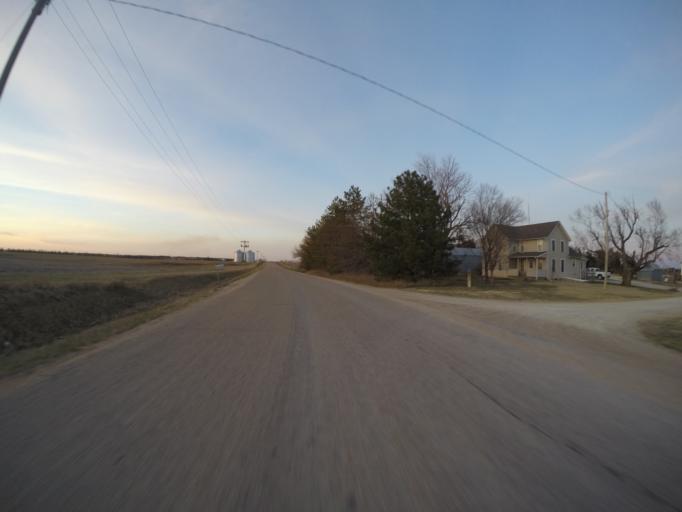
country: US
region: Kansas
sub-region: Washington County
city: Washington
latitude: 39.6107
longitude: -96.9756
